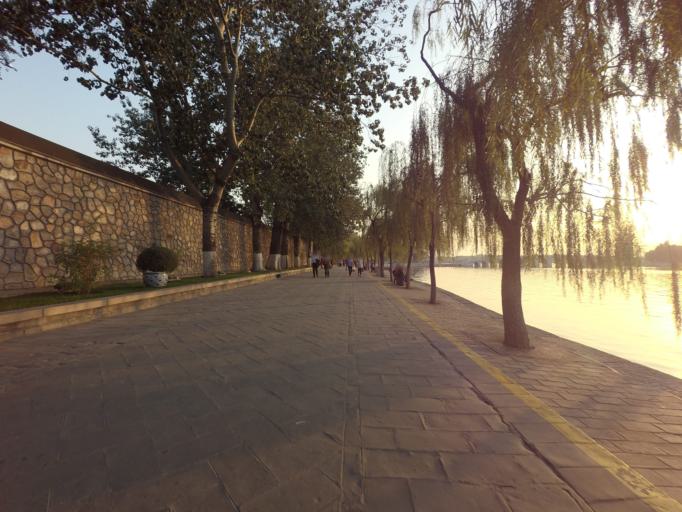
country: CN
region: Beijing
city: Haidian
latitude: 39.9906
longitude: 116.2741
